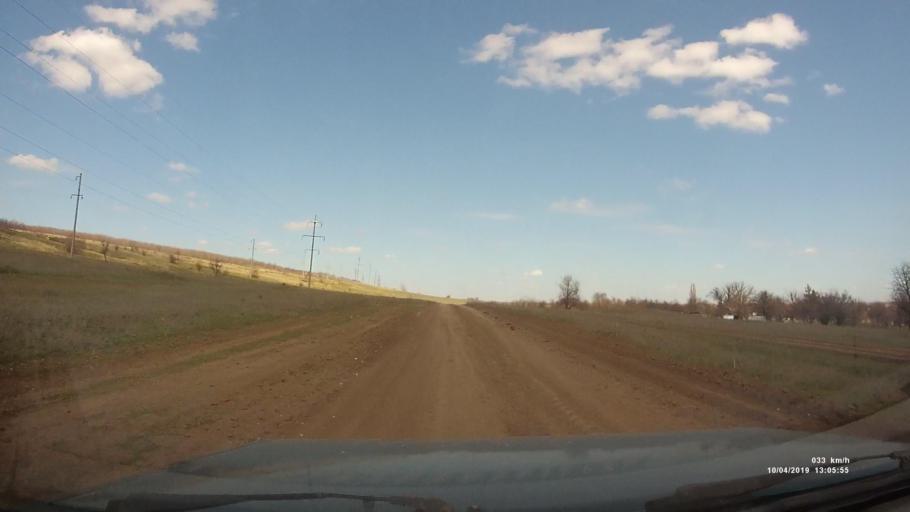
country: RU
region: Rostov
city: Masalovka
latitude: 48.3899
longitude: 40.2341
